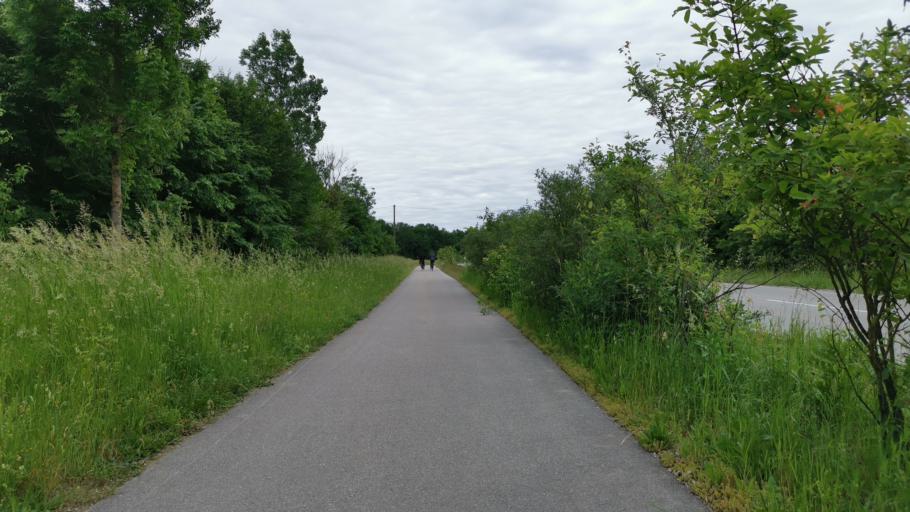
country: DE
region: Bavaria
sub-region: Upper Bavaria
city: Fuerstenfeldbruck
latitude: 48.1905
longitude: 11.2392
